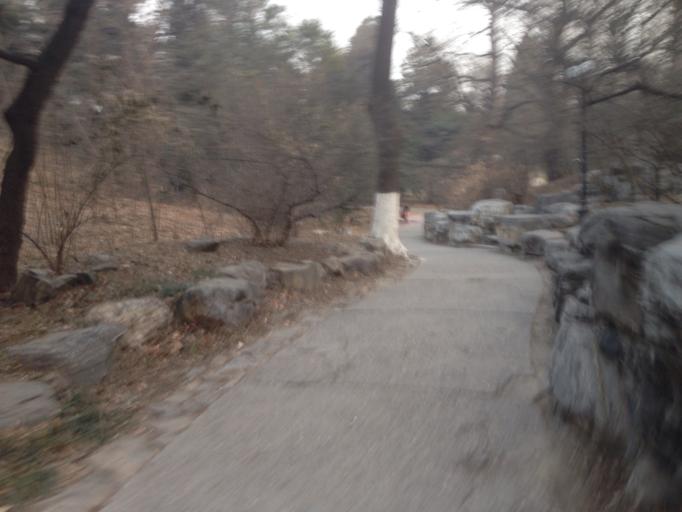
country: CN
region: Beijing
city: Haidian
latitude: 39.9931
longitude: 116.3015
